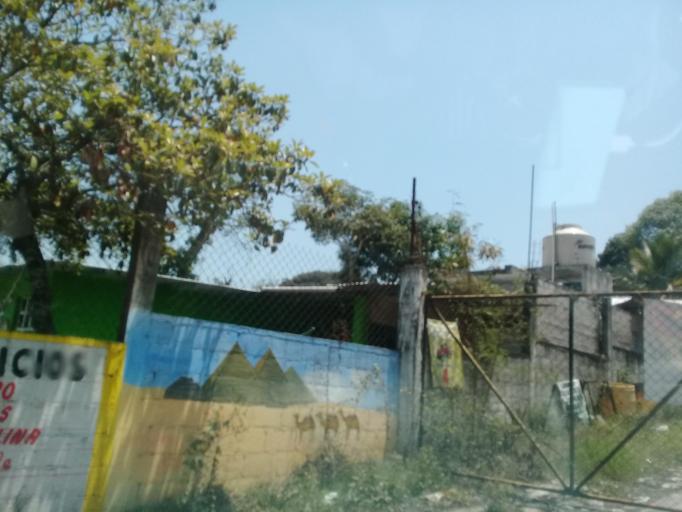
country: MX
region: Veracruz
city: Paraje Nuevo
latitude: 18.8733
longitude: -96.8677
